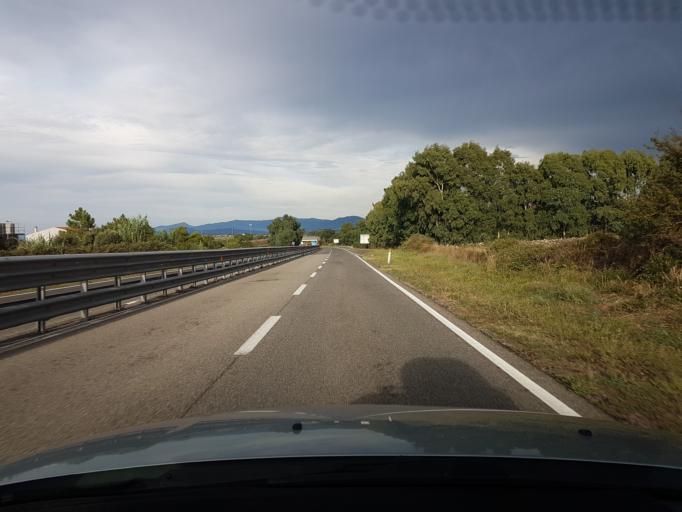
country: IT
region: Sardinia
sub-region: Provincia di Oristano
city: Ghilarza
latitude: 40.1157
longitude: 8.8338
